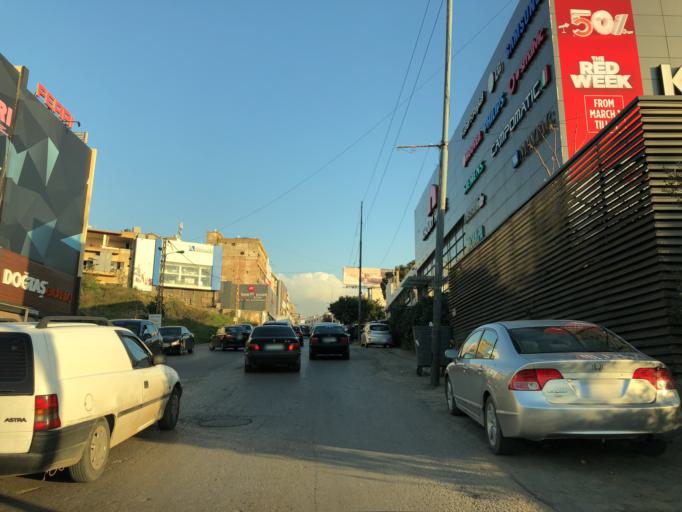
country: LB
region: Mont-Liban
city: Baabda
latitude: 33.8633
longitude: 35.5477
